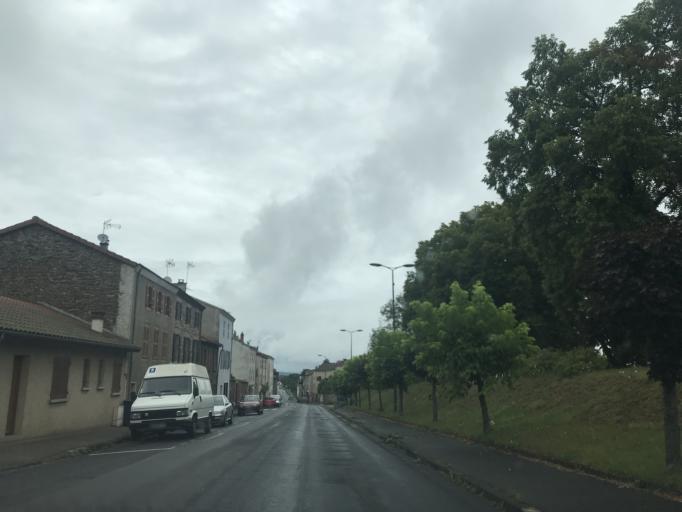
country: FR
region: Auvergne
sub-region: Departement du Puy-de-Dome
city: Arlanc
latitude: 45.4198
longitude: 3.7247
